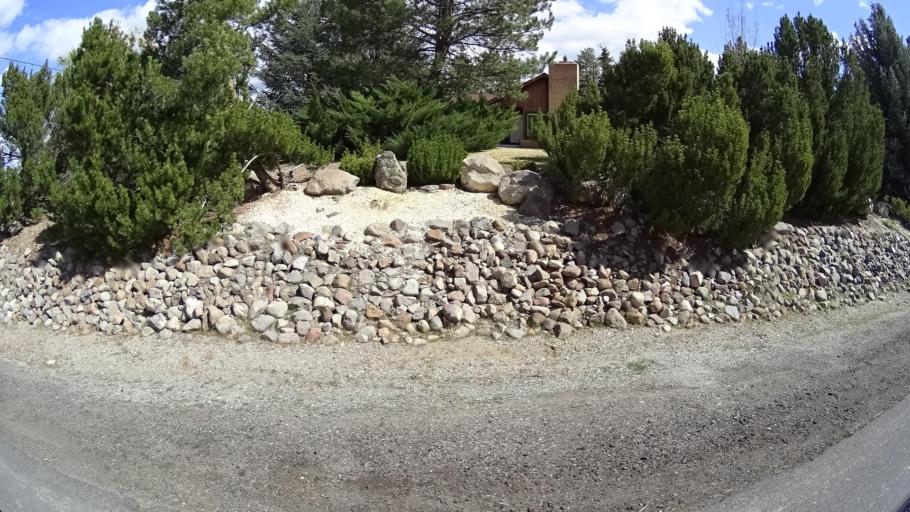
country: US
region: Nevada
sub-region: Washoe County
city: Reno
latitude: 39.4222
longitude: -119.7787
